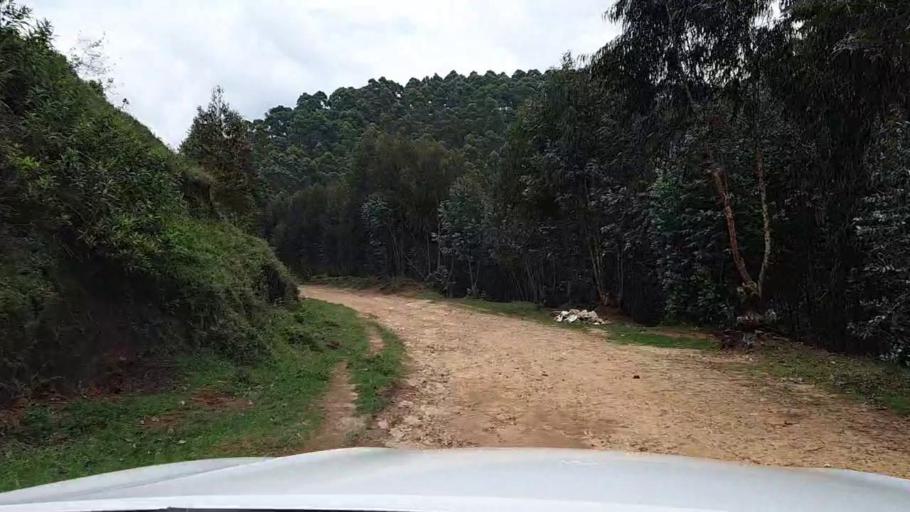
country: RW
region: Western Province
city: Kibuye
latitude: -2.2806
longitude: 29.3682
